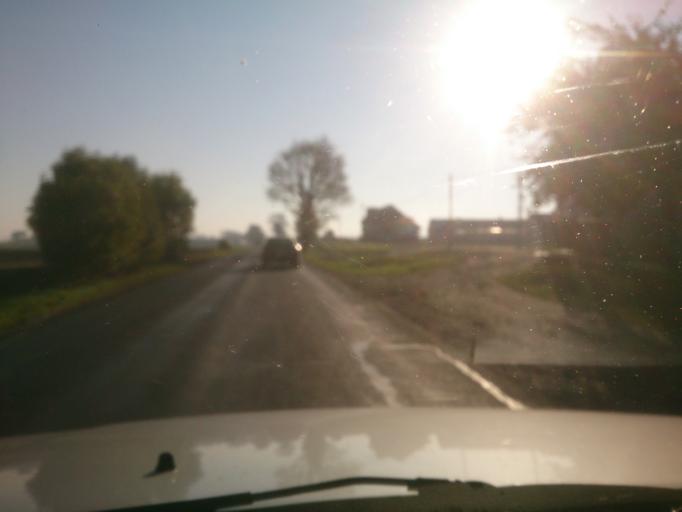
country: PL
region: Kujawsko-Pomorskie
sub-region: Powiat brodnicki
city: Brodnica
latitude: 53.2419
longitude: 19.4839
